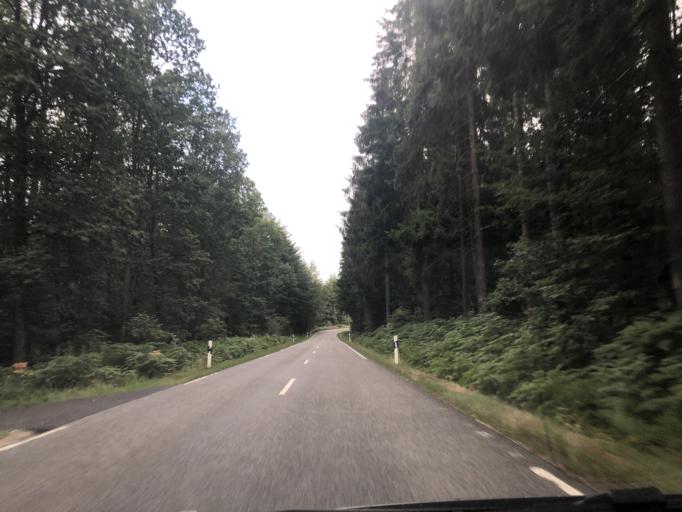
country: DE
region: Rheinland-Pfalz
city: Gusenburg
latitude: 49.6485
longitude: 6.9078
